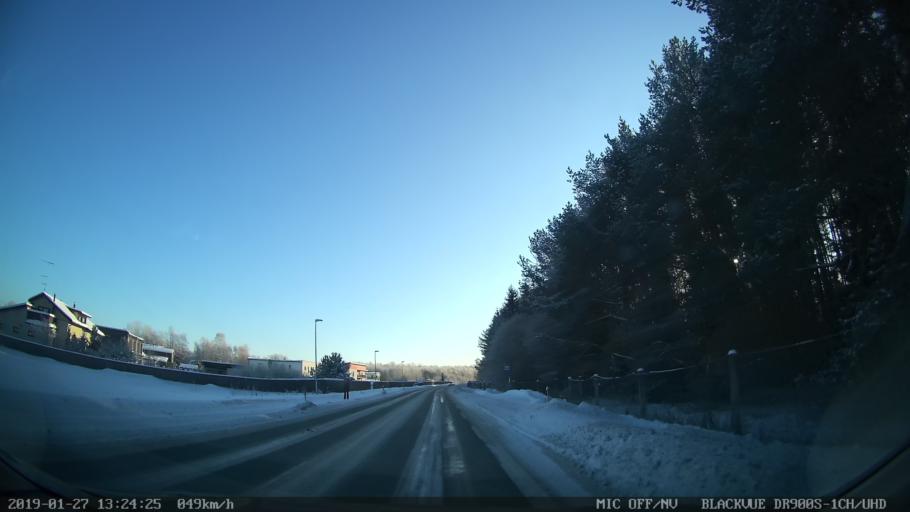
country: EE
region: Harju
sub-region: Tallinna linn
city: Tallinn
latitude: 59.3997
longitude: 24.7911
